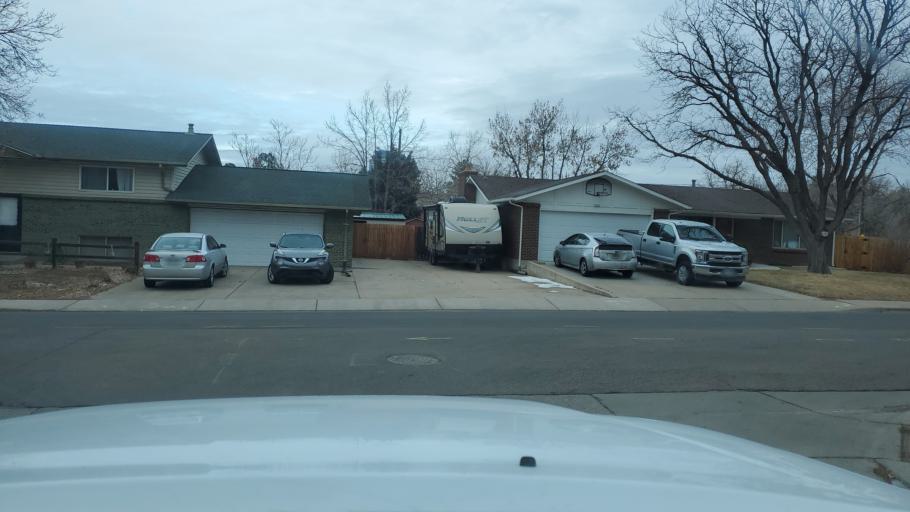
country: US
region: Colorado
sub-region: Arapahoe County
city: Castlewood
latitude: 39.5925
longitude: -104.9000
